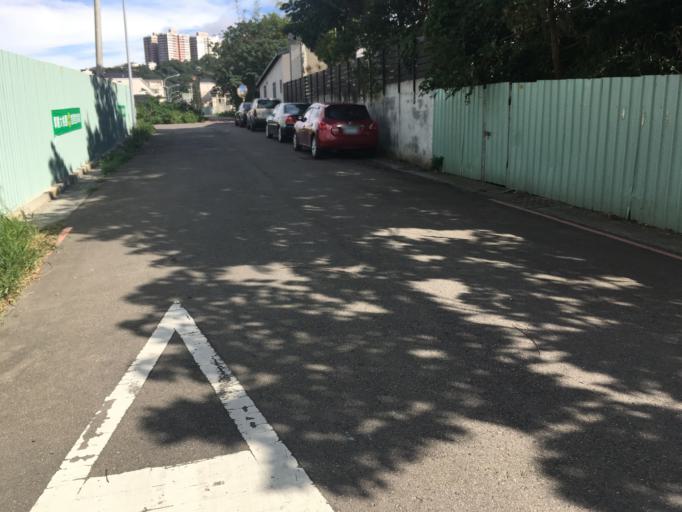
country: TW
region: Taiwan
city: Daxi
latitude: 24.8982
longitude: 121.1484
